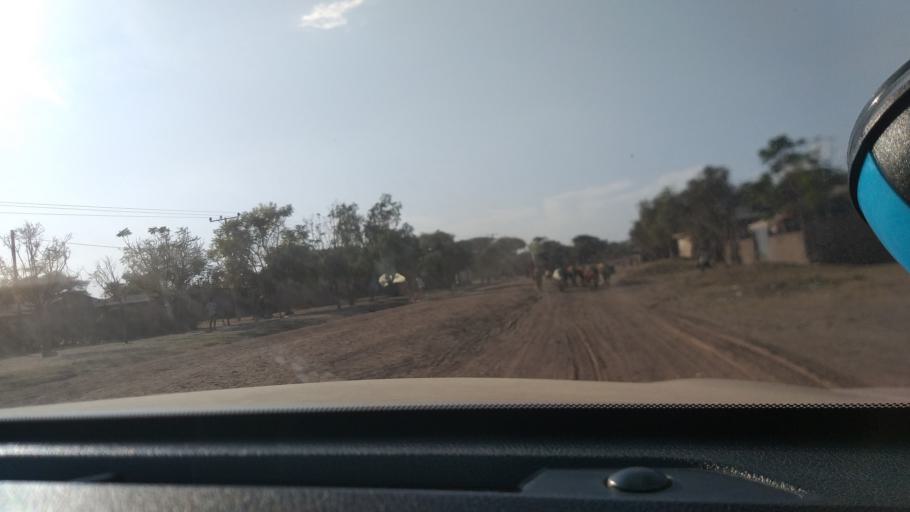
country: ET
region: Oromiya
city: Shashemene
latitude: 7.4902
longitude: 38.7190
